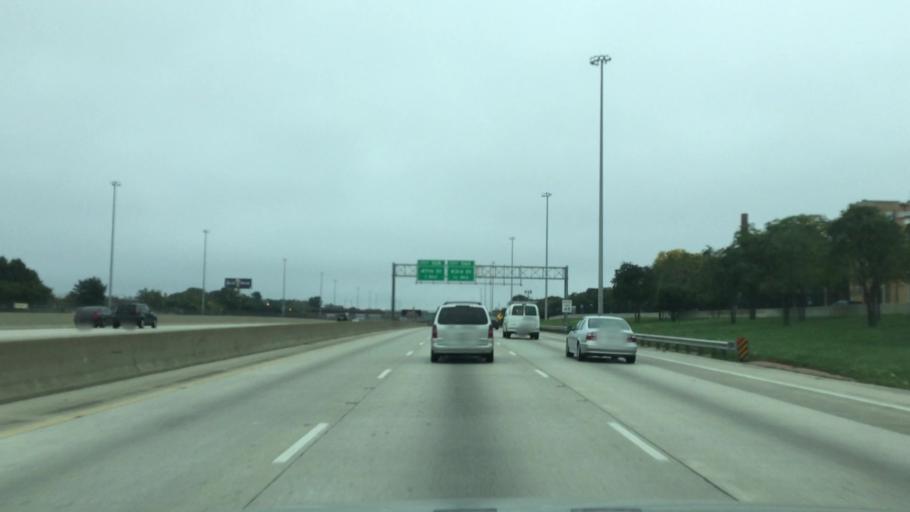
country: US
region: Illinois
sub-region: Cook County
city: Chicago
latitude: 41.8284
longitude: -87.6310
